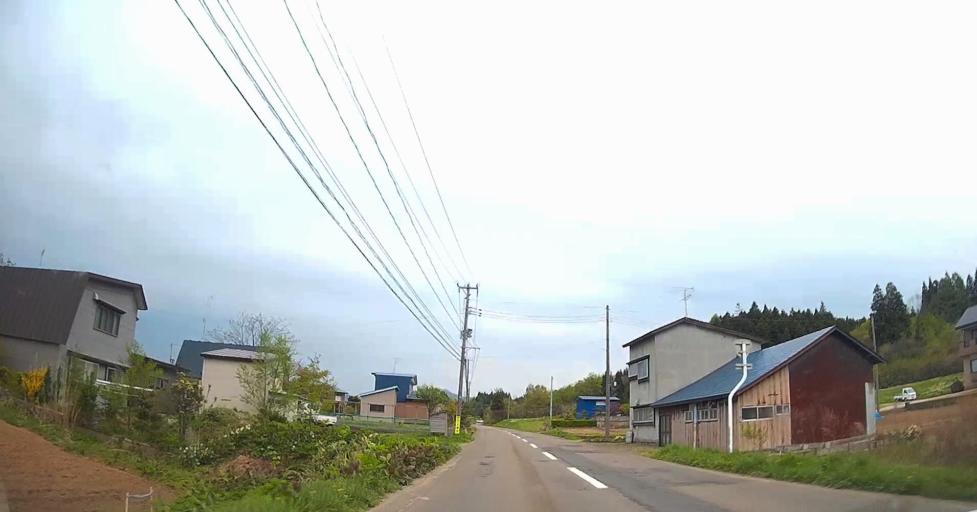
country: JP
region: Aomori
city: Shimokizukuri
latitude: 41.1793
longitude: 140.4653
